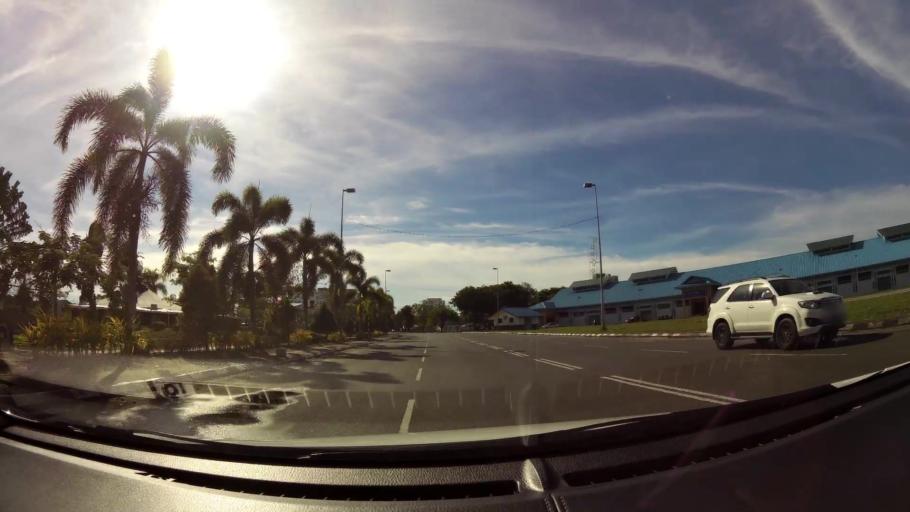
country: BN
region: Belait
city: Kuala Belait
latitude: 4.5798
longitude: 114.1943
